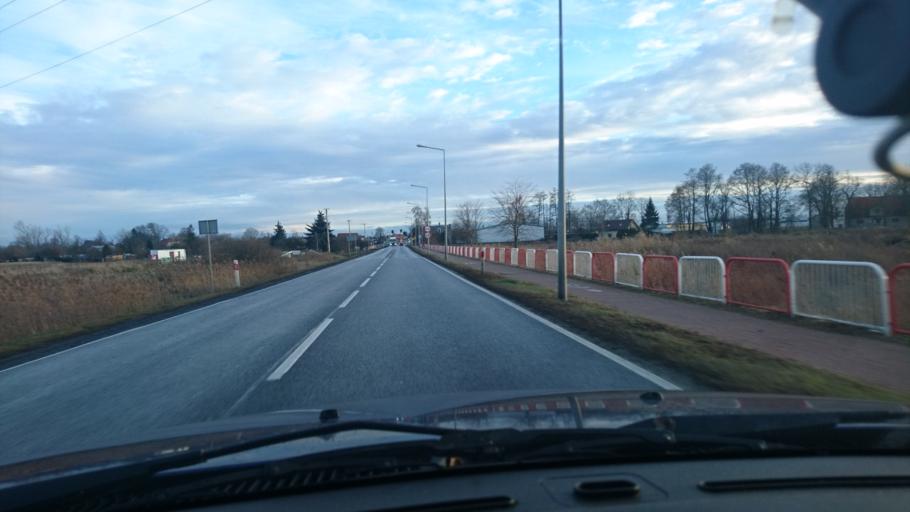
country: PL
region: Greater Poland Voivodeship
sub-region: Powiat kepinski
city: Kepno
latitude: 51.2708
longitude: 17.9946
